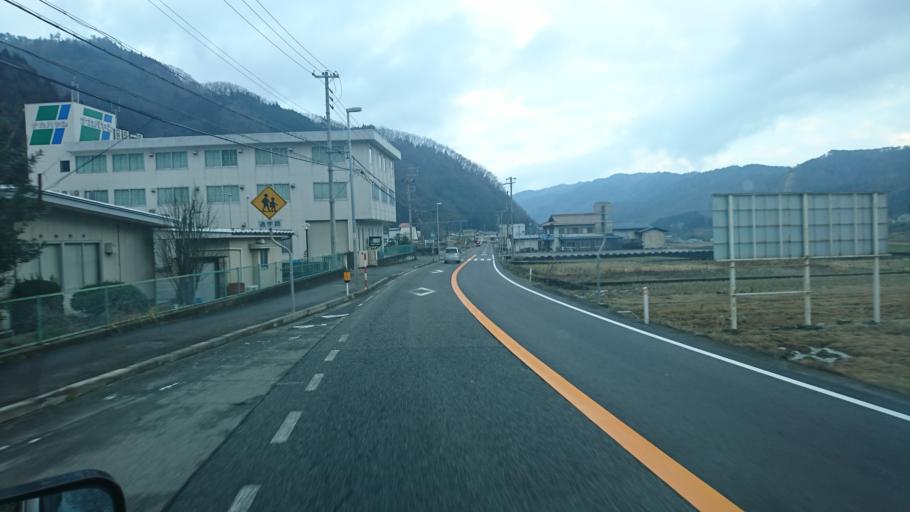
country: JP
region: Hyogo
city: Toyooka
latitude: 35.3875
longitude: 134.6881
